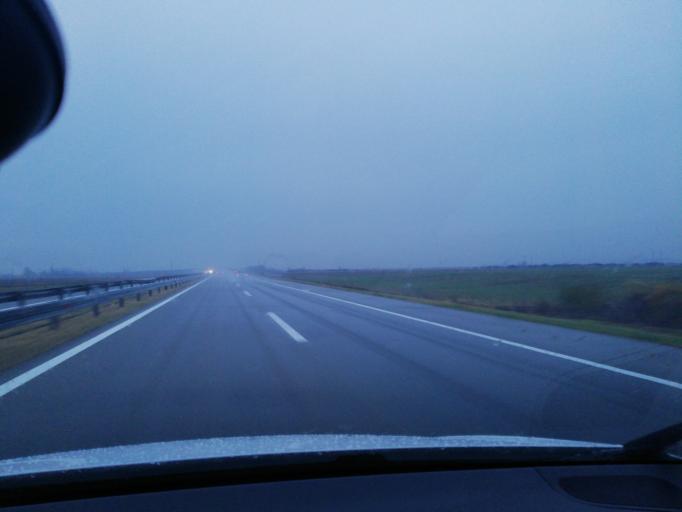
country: RS
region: Autonomna Pokrajina Vojvodina
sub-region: Sremski Okrug
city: Sremska Mitrovica
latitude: 45.0103
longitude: 19.5896
